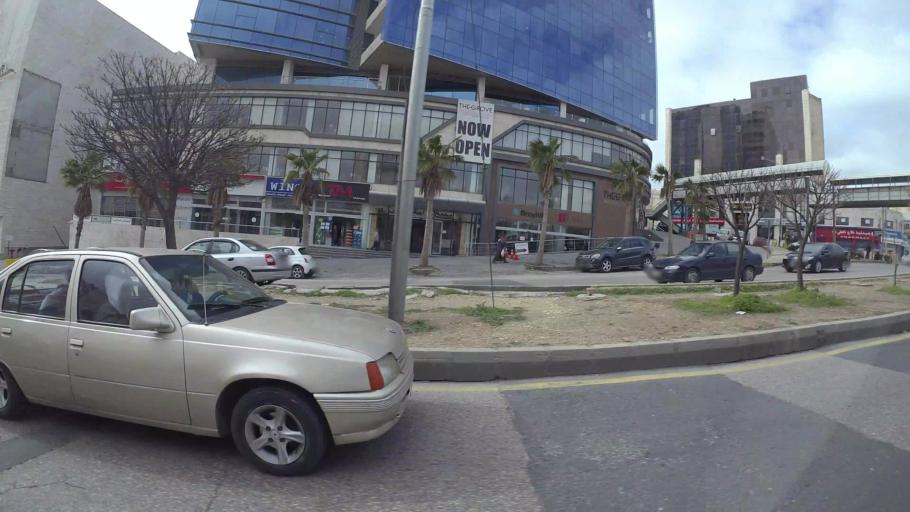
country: JO
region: Amman
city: Al Jubayhah
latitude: 31.9932
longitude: 35.8638
